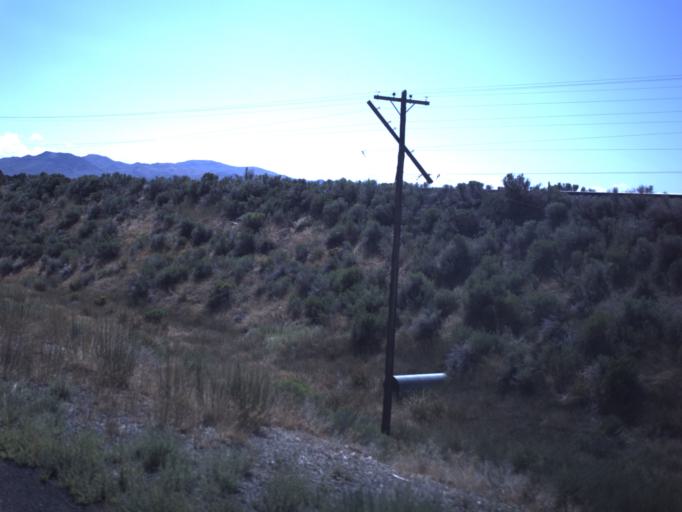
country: US
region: Utah
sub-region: Utah County
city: Genola
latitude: 39.9451
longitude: -112.2277
